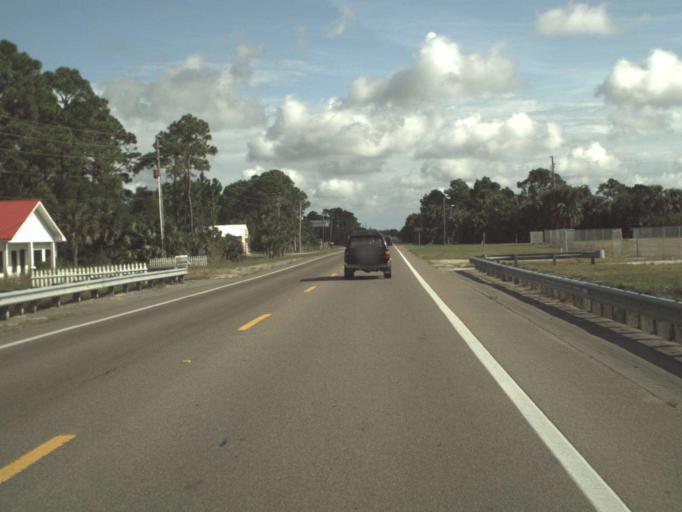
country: US
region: Florida
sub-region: Gulf County
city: Port Saint Joe
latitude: 29.8467
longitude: -85.3266
